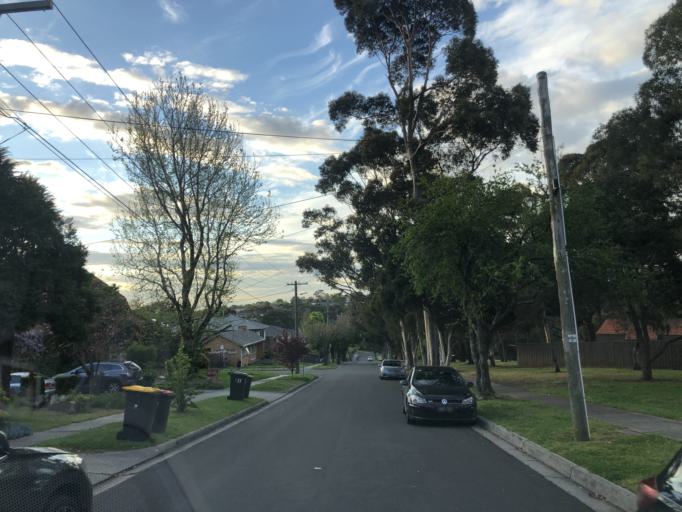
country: AU
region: Victoria
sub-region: Monash
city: Ashwood
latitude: -37.8727
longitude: 145.1274
